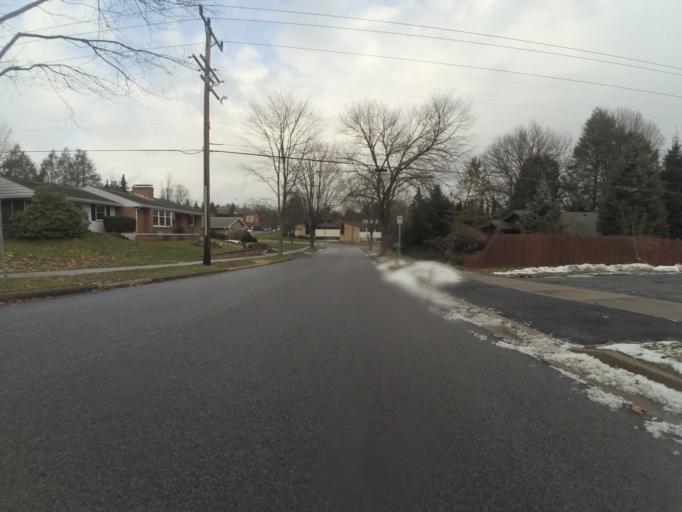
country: US
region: Pennsylvania
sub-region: Centre County
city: State College
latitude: 40.7969
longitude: -77.8454
